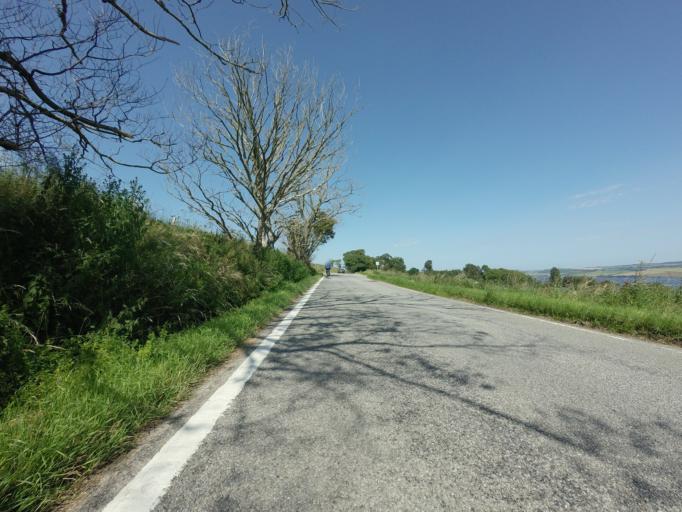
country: GB
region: Scotland
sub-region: Highland
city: Dingwall
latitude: 57.6192
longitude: -4.4027
